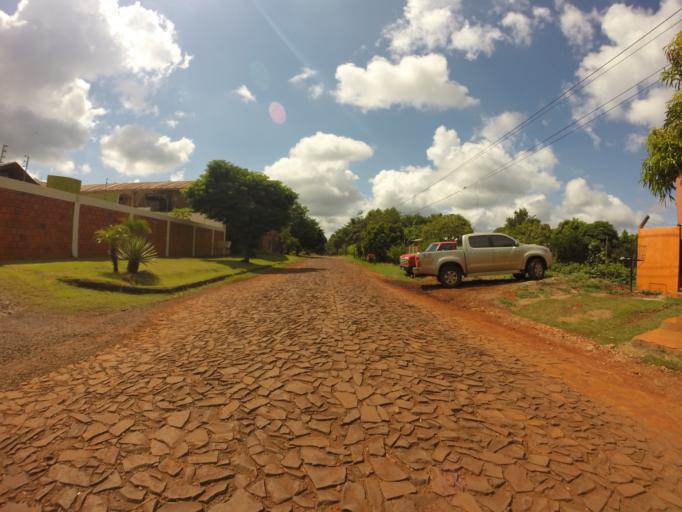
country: PY
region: Alto Parana
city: Ciudad del Este
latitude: -25.3913
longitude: -54.6403
